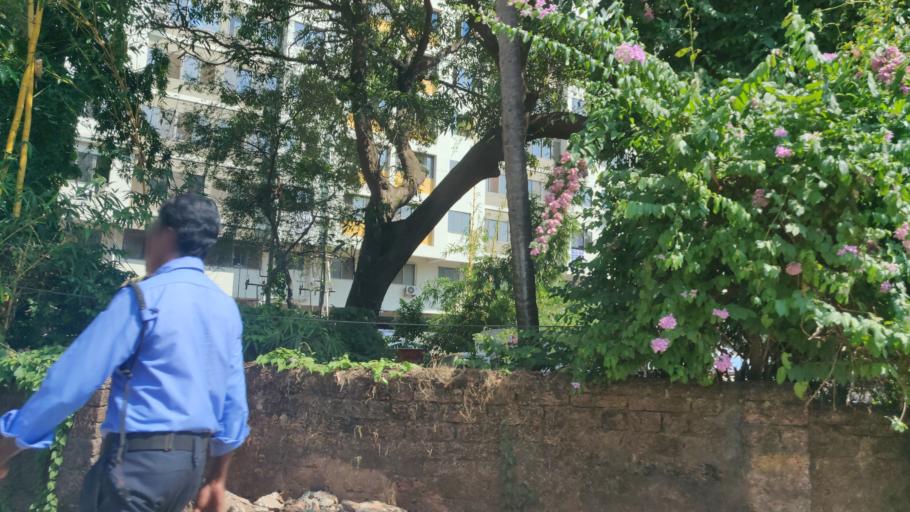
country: IN
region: Karnataka
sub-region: Dakshina Kannada
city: Ullal
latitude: 12.8570
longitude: 74.8369
